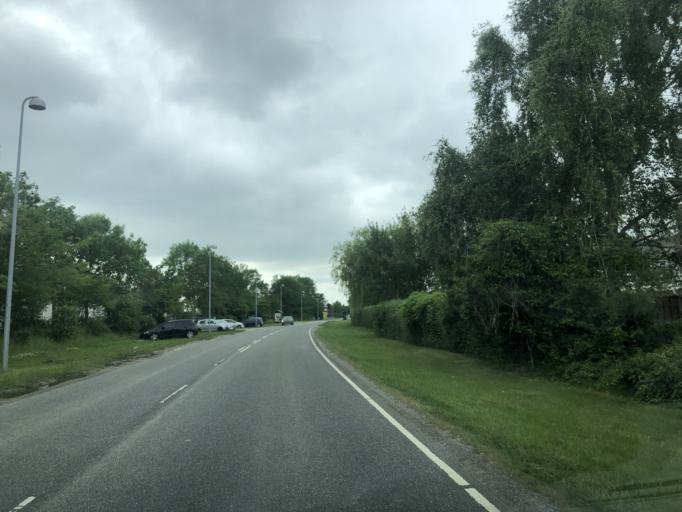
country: DK
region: Capital Region
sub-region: Ishoj Kommune
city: Ishoj
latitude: 55.6041
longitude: 12.3300
